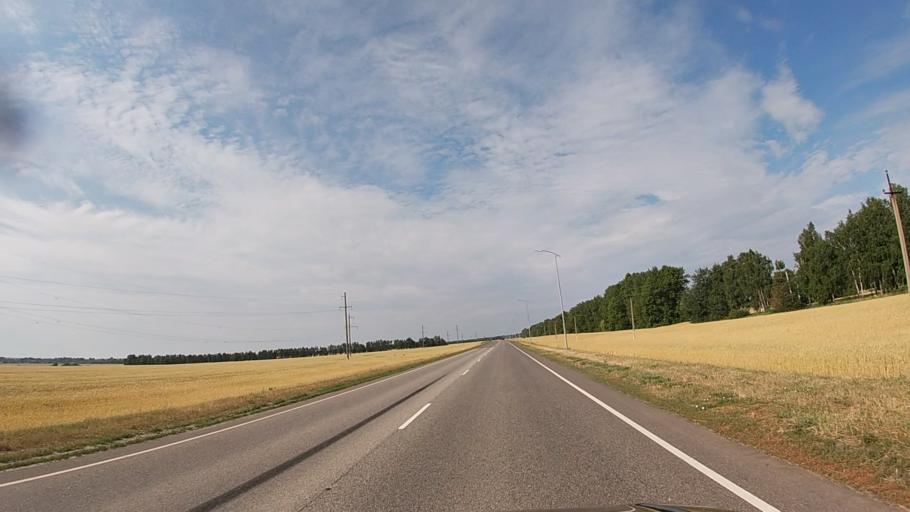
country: RU
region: Belgorod
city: Proletarskiy
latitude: 50.8181
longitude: 35.7543
